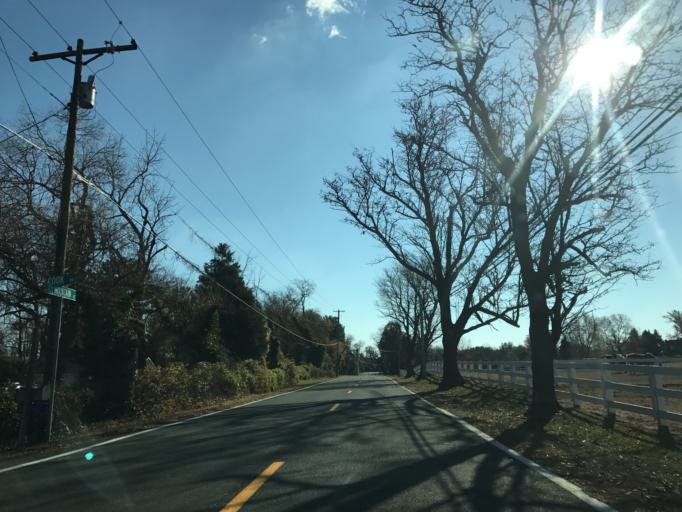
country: US
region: Maryland
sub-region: Anne Arundel County
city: Cape Saint Claire
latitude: 39.0942
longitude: -76.4287
